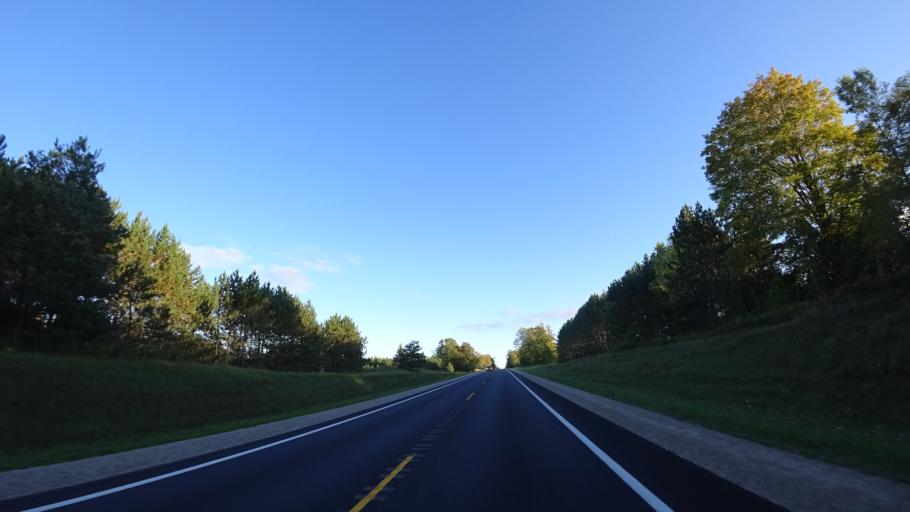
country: US
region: Michigan
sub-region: Luce County
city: Newberry
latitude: 46.3261
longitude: -85.6719
